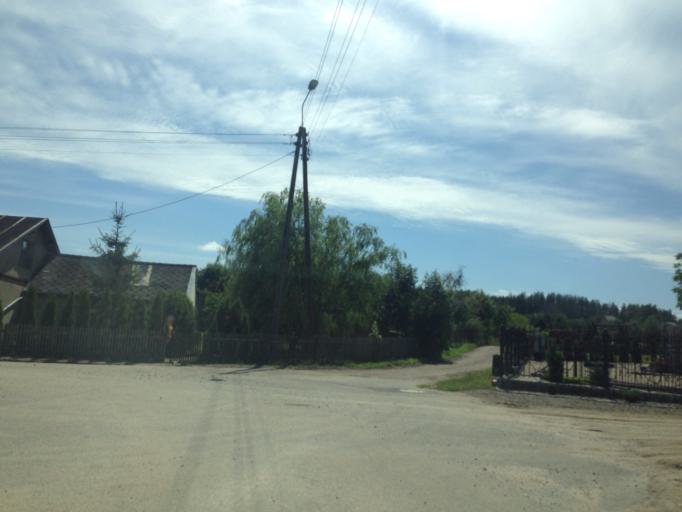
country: PL
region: Pomeranian Voivodeship
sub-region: Powiat koscierski
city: Karsin
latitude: 53.9490
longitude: 17.8712
